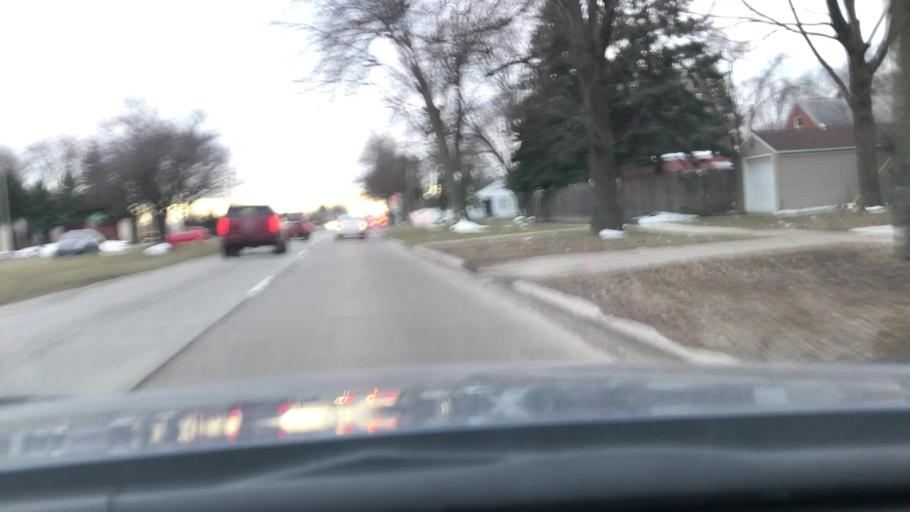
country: US
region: Michigan
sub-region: Oakland County
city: Birmingham
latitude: 42.5502
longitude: -83.1865
